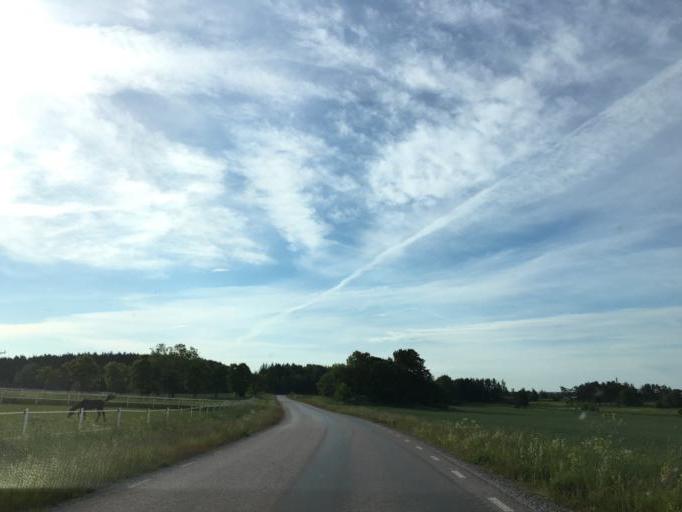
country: SE
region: Soedermanland
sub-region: Eskilstuna Kommun
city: Torshalla
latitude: 59.4172
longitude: 16.4379
